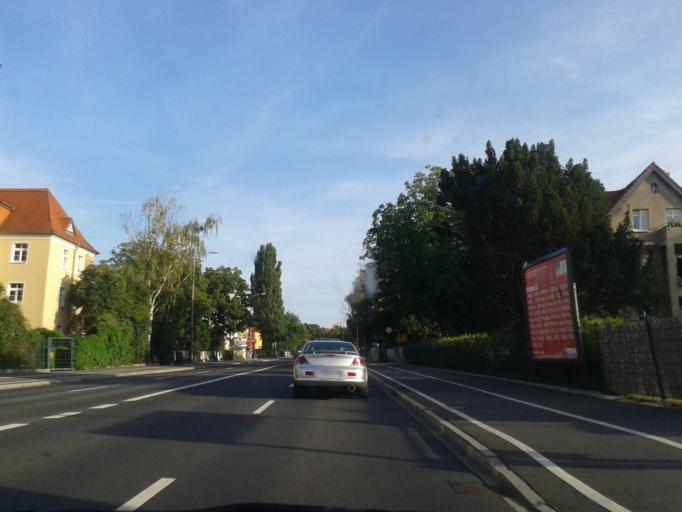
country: DE
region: Saxony
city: Dresden
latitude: 51.0179
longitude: 13.7697
